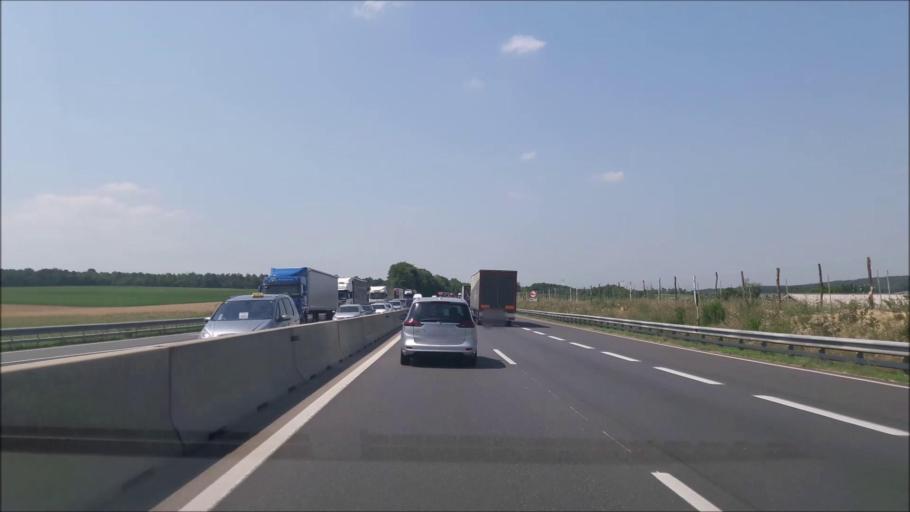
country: AT
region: Lower Austria
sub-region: Politischer Bezirk Bruck an der Leitha
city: Bruck an der Leitha
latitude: 48.0591
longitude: 16.7078
